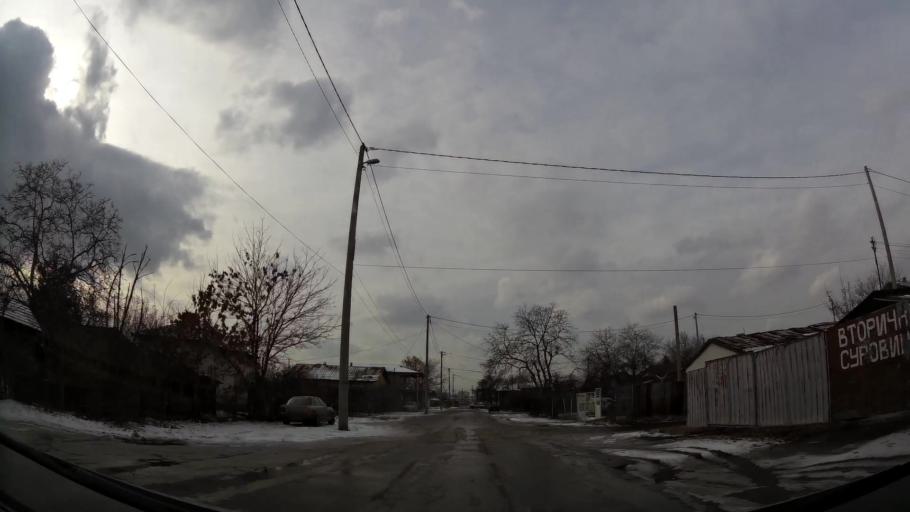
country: BG
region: Sofia-Capital
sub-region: Stolichna Obshtina
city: Sofia
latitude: 42.6915
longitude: 23.3878
